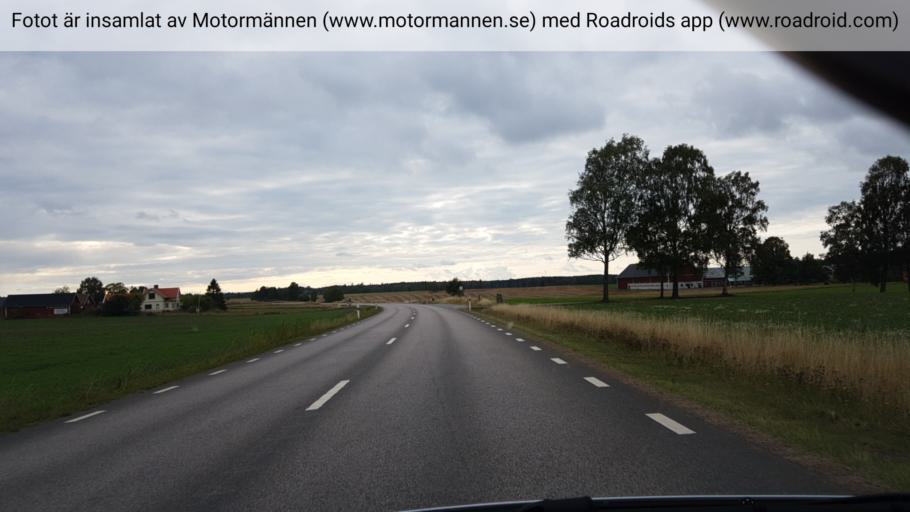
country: SE
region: Vaestra Goetaland
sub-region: Tibro Kommun
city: Tibro
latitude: 58.3466
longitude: 14.1449
